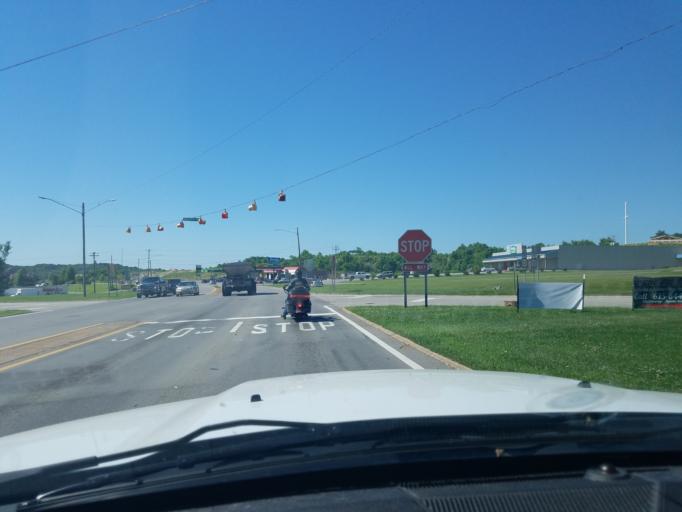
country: US
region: Tennessee
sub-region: Sumner County
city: Westmoreland
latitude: 36.5589
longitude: -86.2402
